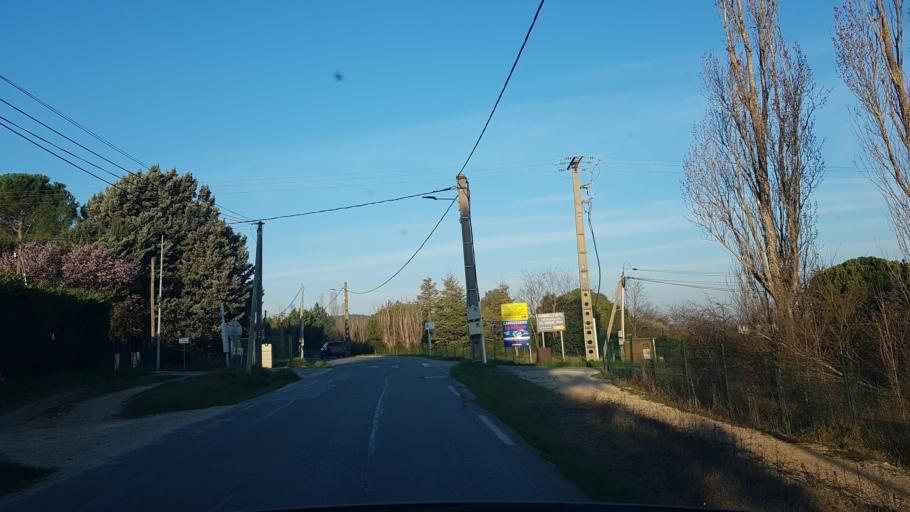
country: FR
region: Provence-Alpes-Cote d'Azur
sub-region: Departement des Bouches-du-Rhone
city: Cabries
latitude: 43.4488
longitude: 5.3854
